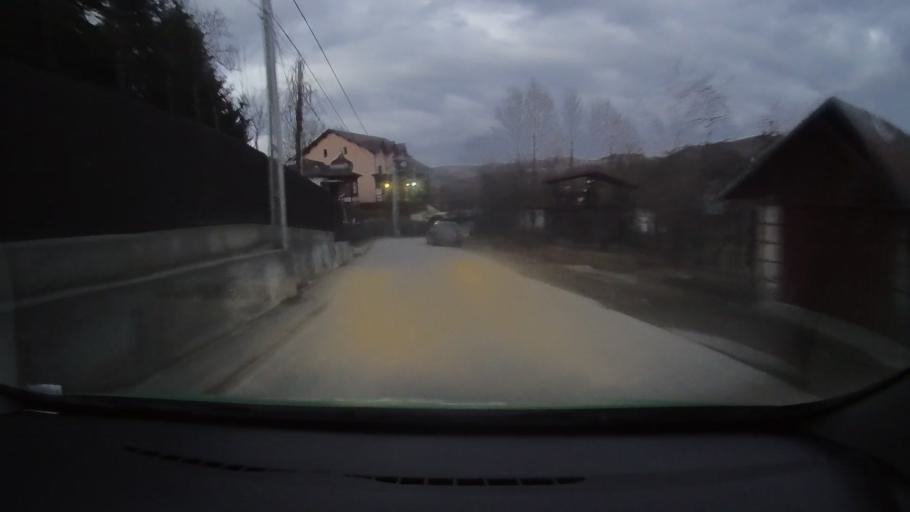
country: RO
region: Prahova
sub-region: Comuna Provita de Sus
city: Provita de Sus
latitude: 45.1388
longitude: 25.6258
